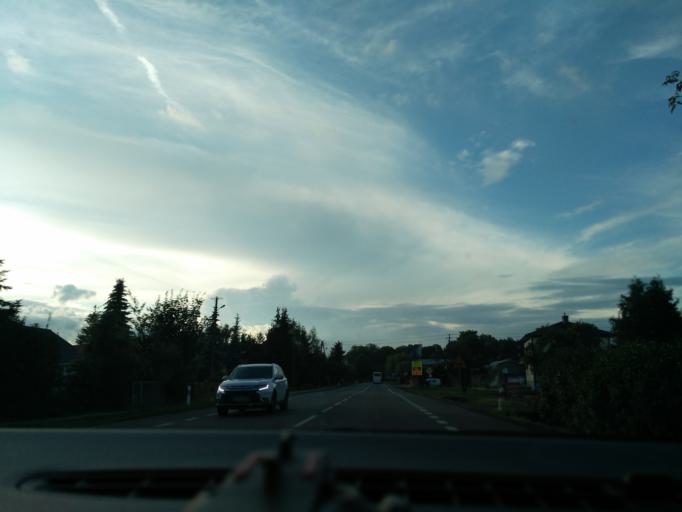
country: PL
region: Lublin Voivodeship
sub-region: Powiat lubelski
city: Niedrzwica Duza
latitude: 51.0883
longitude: 22.3671
